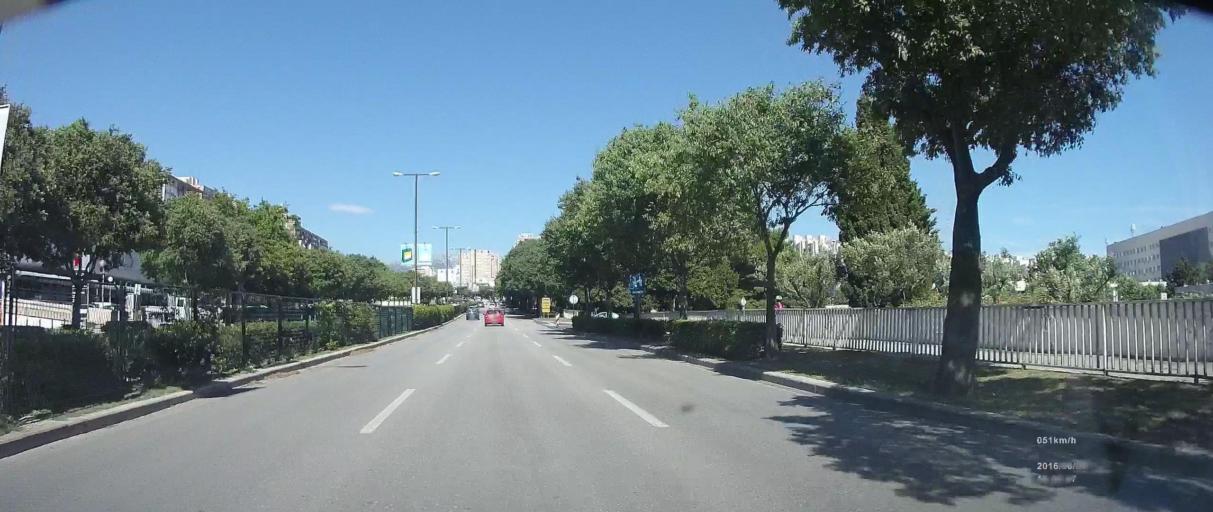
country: HR
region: Splitsko-Dalmatinska
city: Vranjic
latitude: 43.5069
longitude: 16.4667
